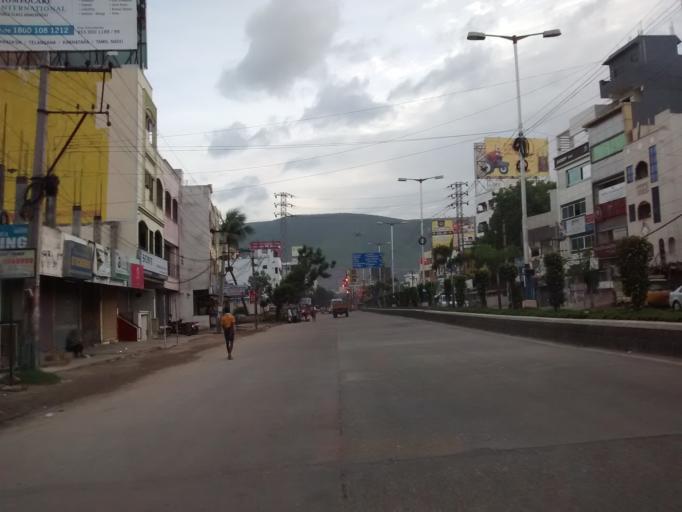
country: IN
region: Andhra Pradesh
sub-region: Chittoor
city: Tirupati
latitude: 13.6403
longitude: 79.4276
